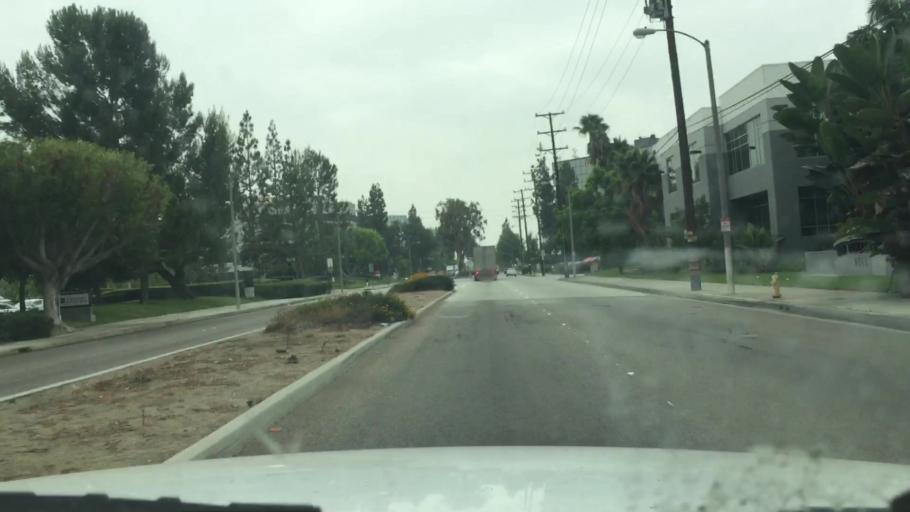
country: US
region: California
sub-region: Los Angeles County
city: Commerce
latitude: 33.9884
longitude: -118.1617
